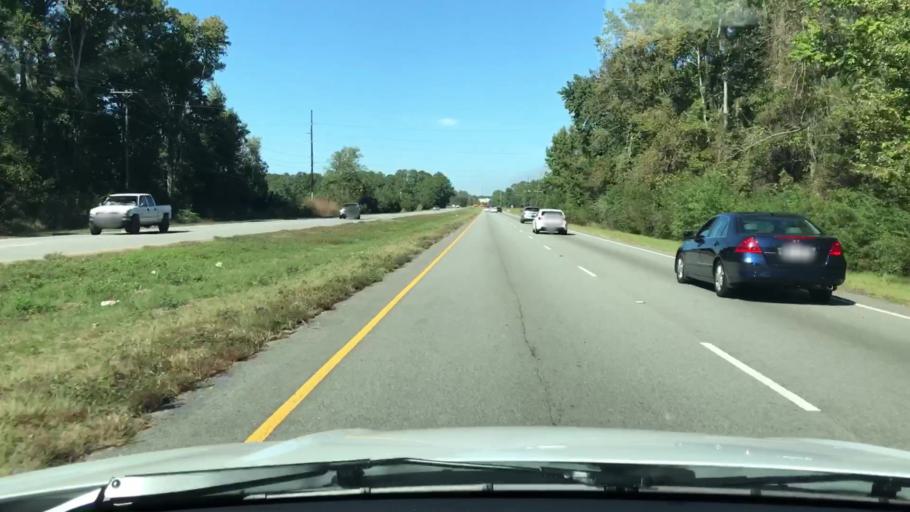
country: US
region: South Carolina
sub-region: Beaufort County
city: Laurel Bay
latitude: 32.4991
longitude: -80.7435
